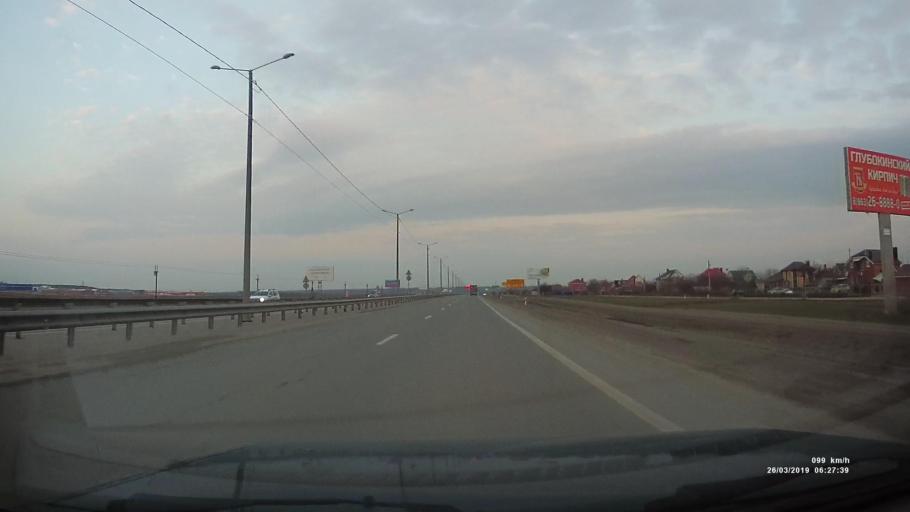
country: RU
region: Rostov
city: Kalinin
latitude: 47.2615
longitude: 39.6084
